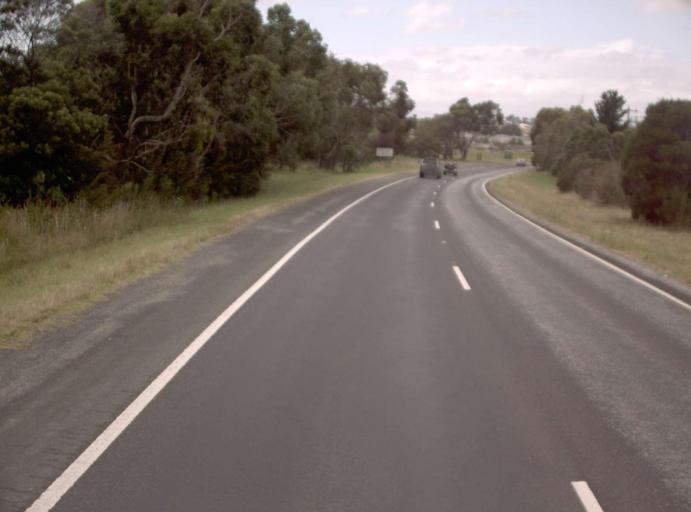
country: AU
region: Victoria
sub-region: Cardinia
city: Pakenham Upper
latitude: -38.0666
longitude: 145.4993
